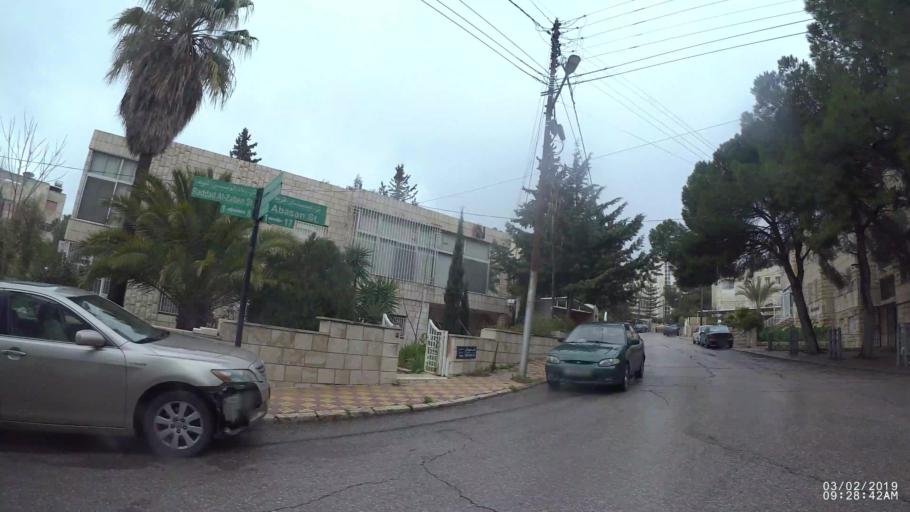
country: JO
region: Amman
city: Amman
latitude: 31.9491
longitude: 35.9066
